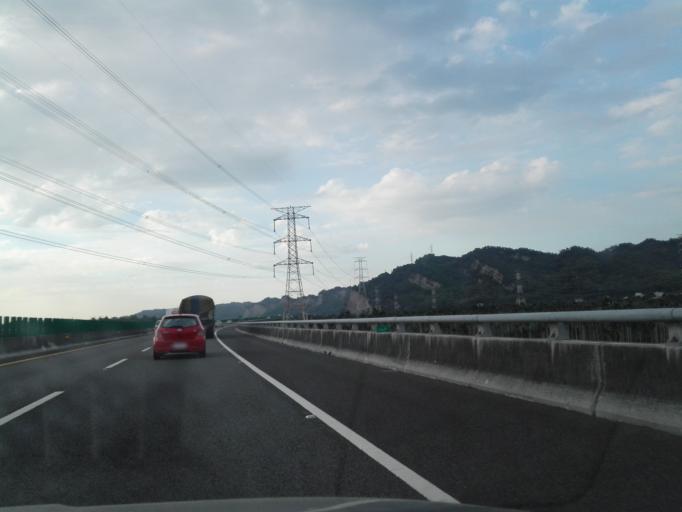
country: TW
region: Taiwan
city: Zhongxing New Village
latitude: 23.9859
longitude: 120.7579
